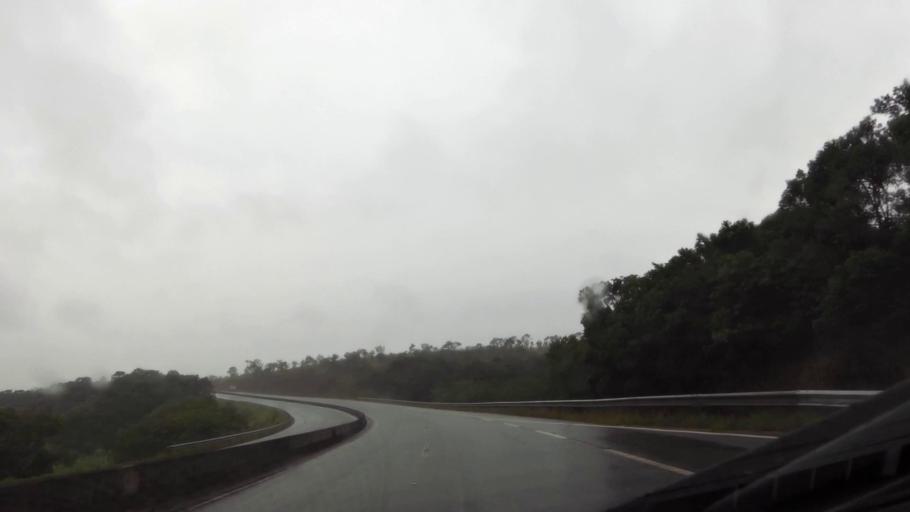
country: BR
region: Espirito Santo
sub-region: Guarapari
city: Guarapari
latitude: -20.6271
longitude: -40.5033
